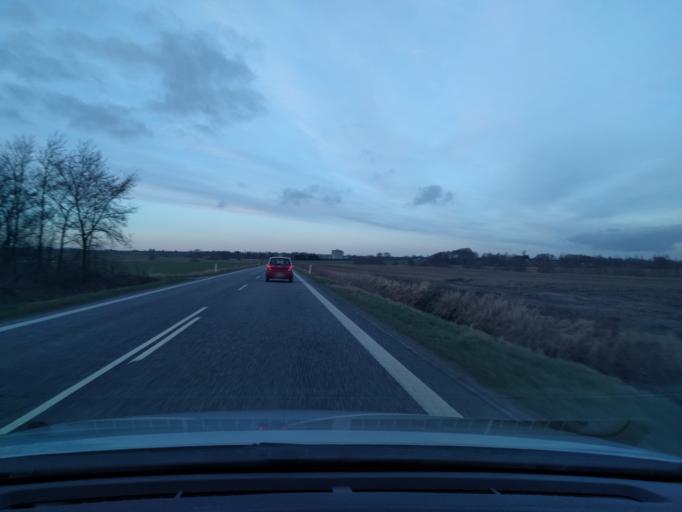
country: DK
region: South Denmark
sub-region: Tonder Kommune
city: Toftlund
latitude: 55.1607
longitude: 9.0425
